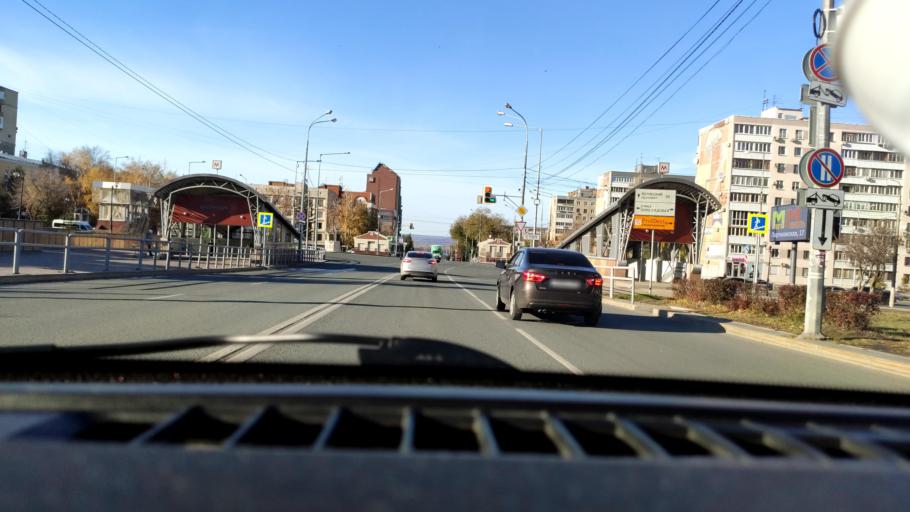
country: RU
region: Samara
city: Samara
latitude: 53.2085
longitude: 50.1344
